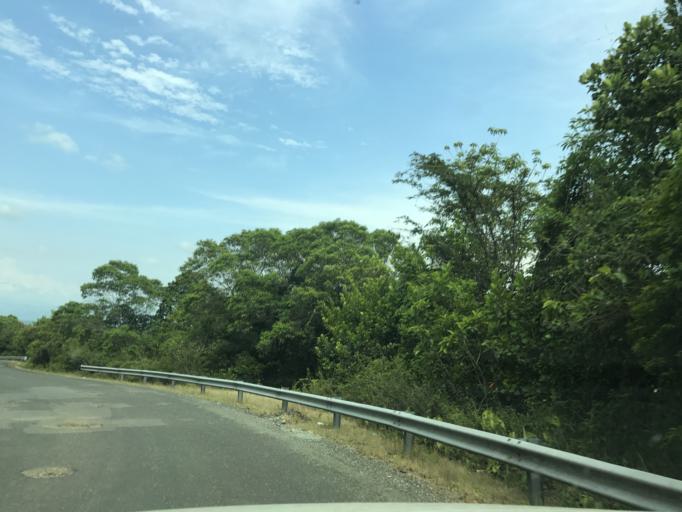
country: GT
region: Izabal
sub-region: Municipio de Los Amates
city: Los Amates
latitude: 15.3854
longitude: -89.0243
